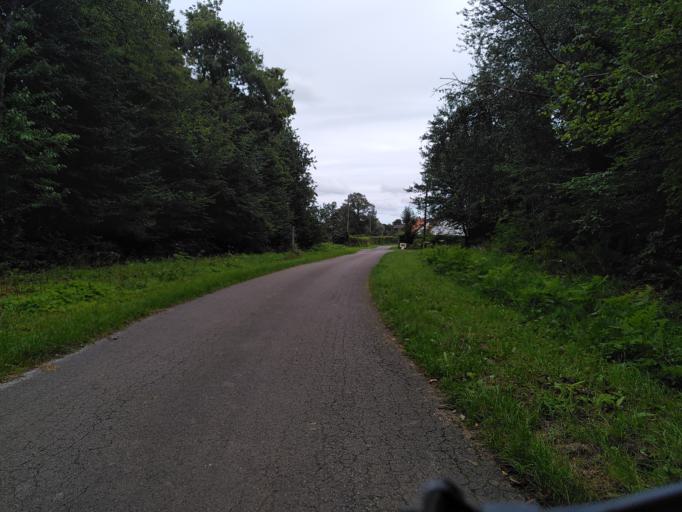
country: FR
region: Nord-Pas-de-Calais
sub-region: Departement du Pas-de-Calais
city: Desvres
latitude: 50.6812
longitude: 1.8454
